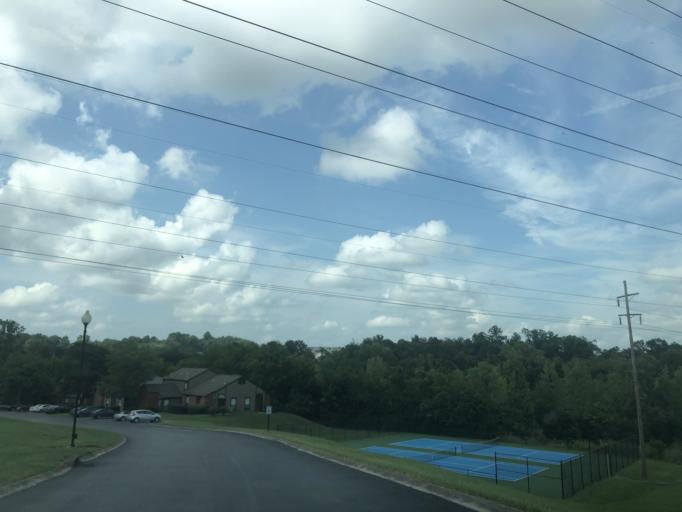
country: US
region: Tennessee
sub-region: Davidson County
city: Lakewood
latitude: 36.1597
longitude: -86.6256
